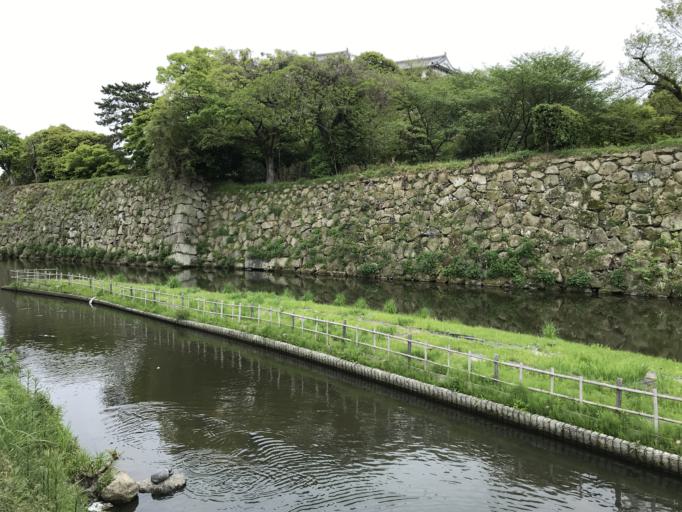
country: JP
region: Hyogo
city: Himeji
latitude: 34.8391
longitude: 134.6897
